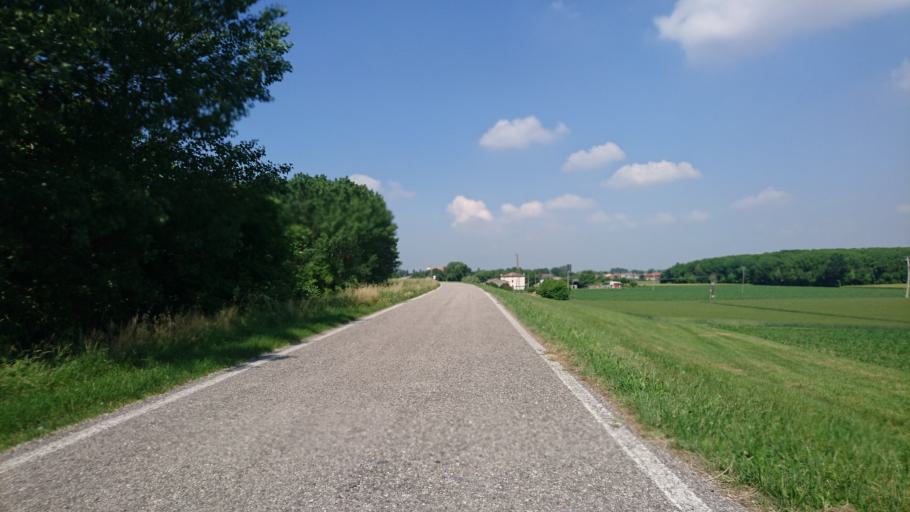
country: IT
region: Lombardy
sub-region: Provincia di Mantova
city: San Benedetto Po
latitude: 45.0787
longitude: 10.9704
